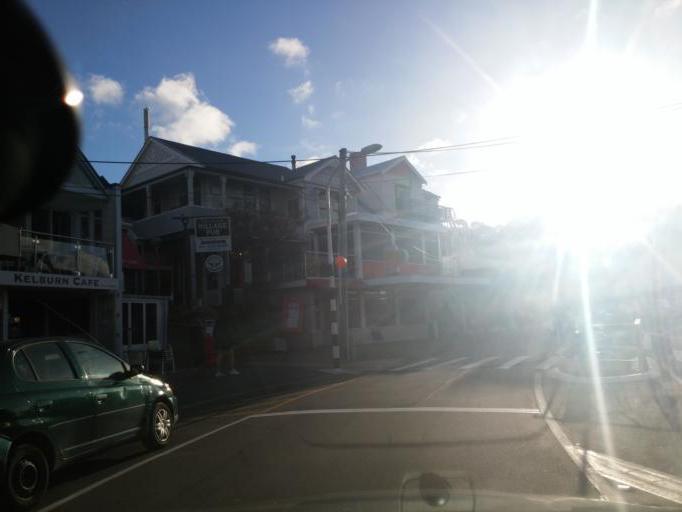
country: NZ
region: Wellington
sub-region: Wellington City
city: Kelburn
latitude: -41.2894
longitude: 174.7626
